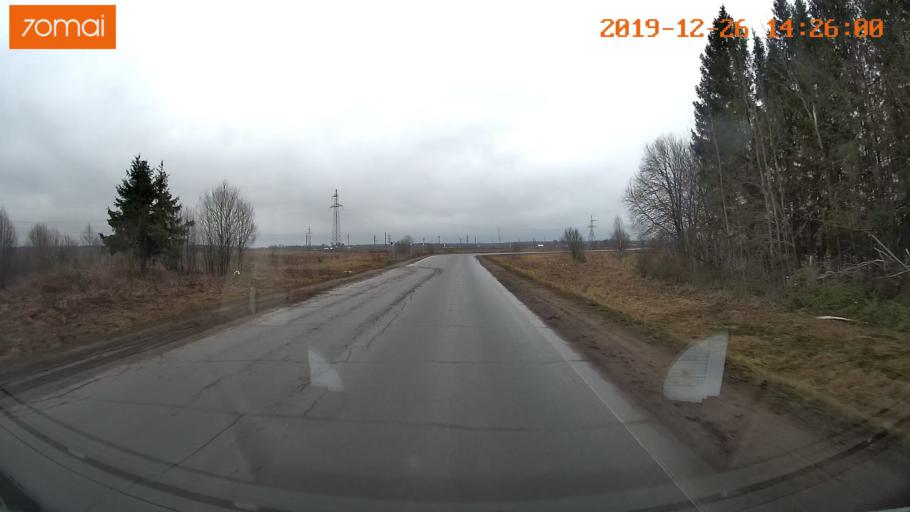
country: RU
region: Jaroslavl
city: Poshekhon'ye
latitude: 58.4895
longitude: 39.0911
